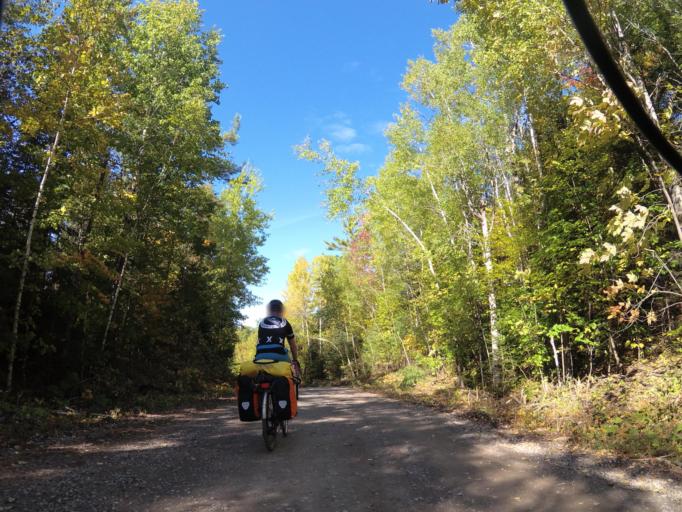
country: CA
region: Ontario
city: Renfrew
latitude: 45.3350
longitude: -77.0546
